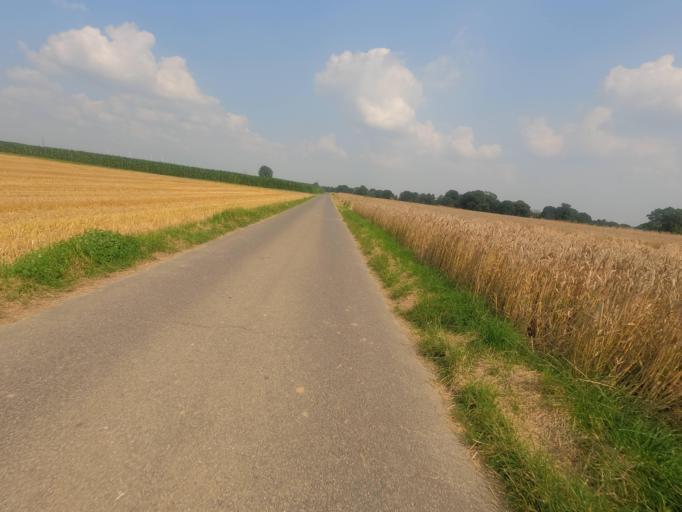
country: DE
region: North Rhine-Westphalia
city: Baesweiler
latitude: 50.9390
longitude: 6.1751
